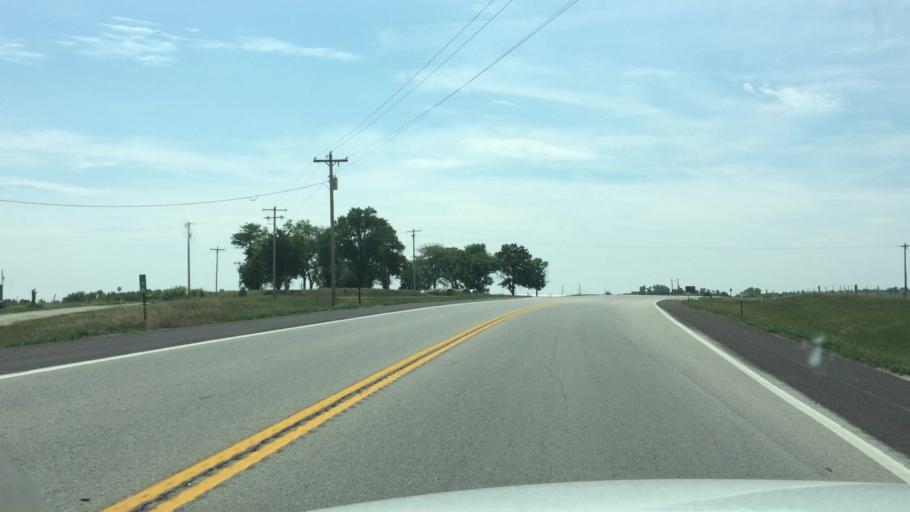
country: US
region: Kansas
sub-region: Jackson County
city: Holton
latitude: 39.5673
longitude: -95.7333
